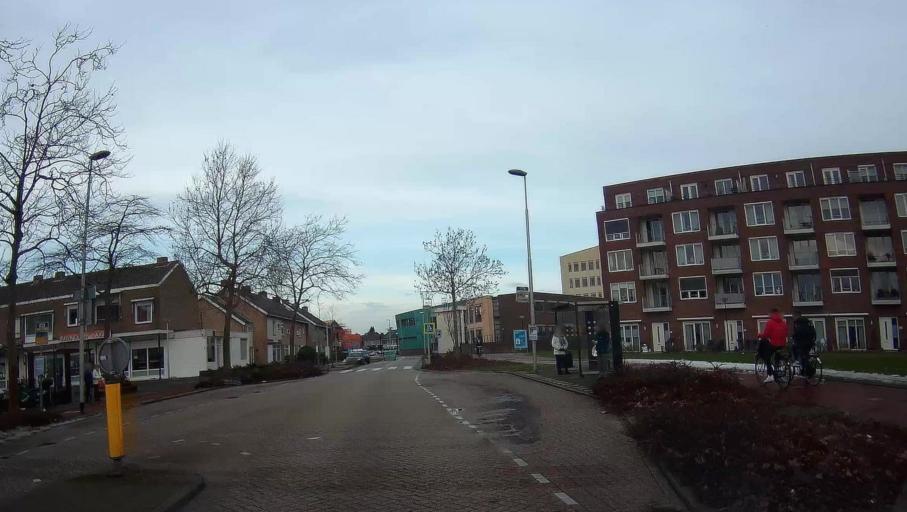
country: NL
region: South Holland
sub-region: Gemeente Barendrecht
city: Barendrecht
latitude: 51.8557
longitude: 4.5400
